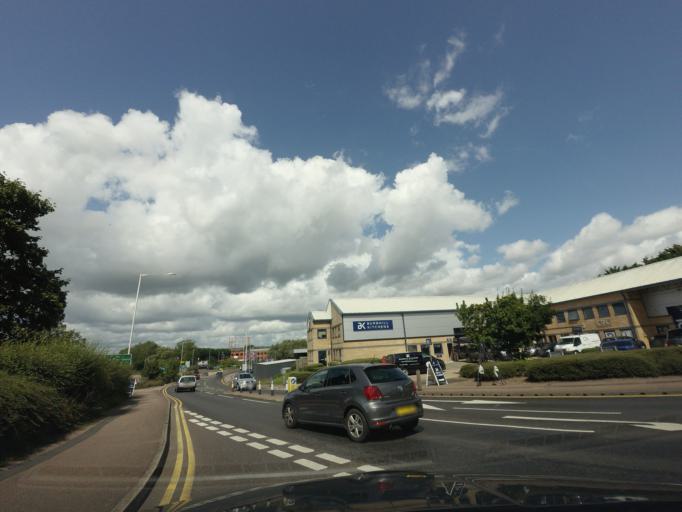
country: GB
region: England
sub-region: Kent
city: Tonbridge
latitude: 51.1907
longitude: 0.2880
